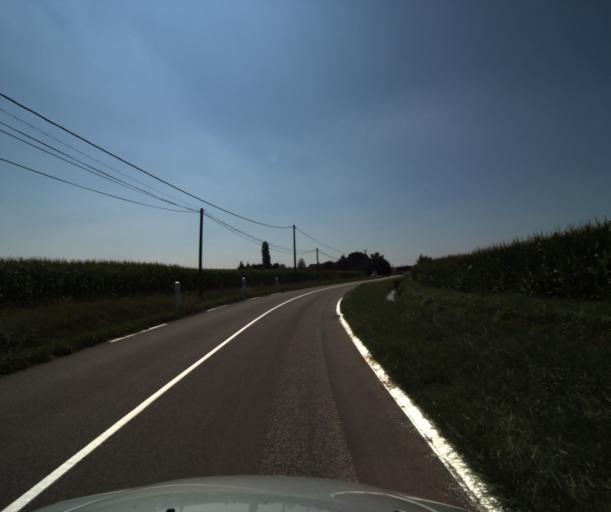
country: FR
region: Midi-Pyrenees
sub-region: Departement de la Haute-Garonne
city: Labastidette
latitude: 43.4376
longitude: 1.2549
